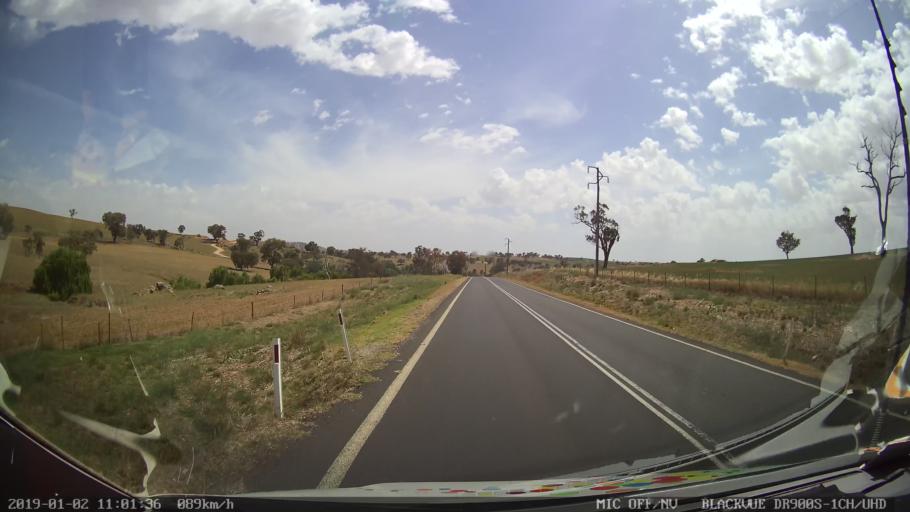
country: AU
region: New South Wales
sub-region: Young
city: Young
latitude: -34.5960
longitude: 148.3210
